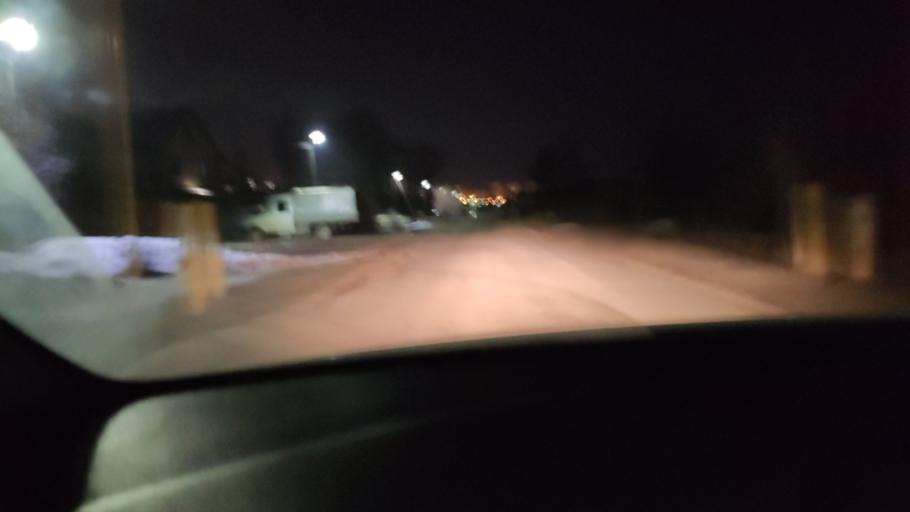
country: RU
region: Tatarstan
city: Stolbishchi
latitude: 55.7602
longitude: 49.2618
